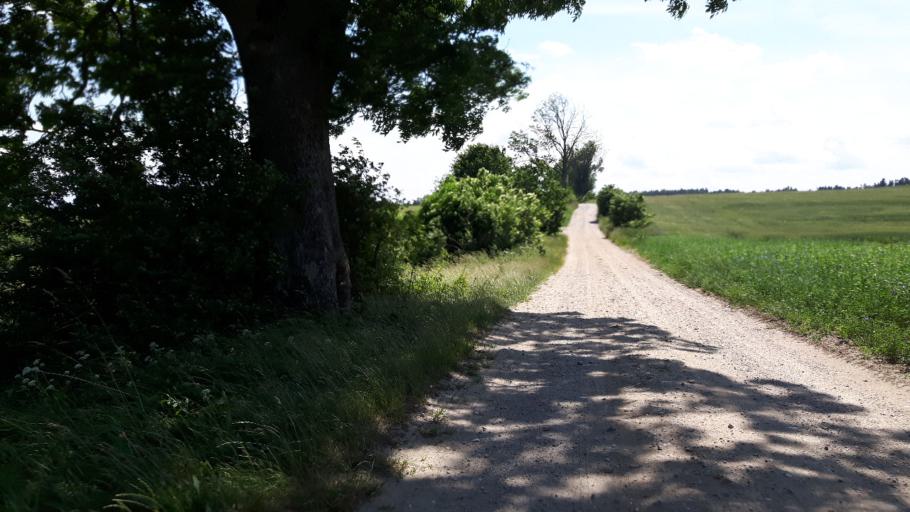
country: PL
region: Pomeranian Voivodeship
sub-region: Powiat wejherowski
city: Choczewo
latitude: 54.7483
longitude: 17.9463
